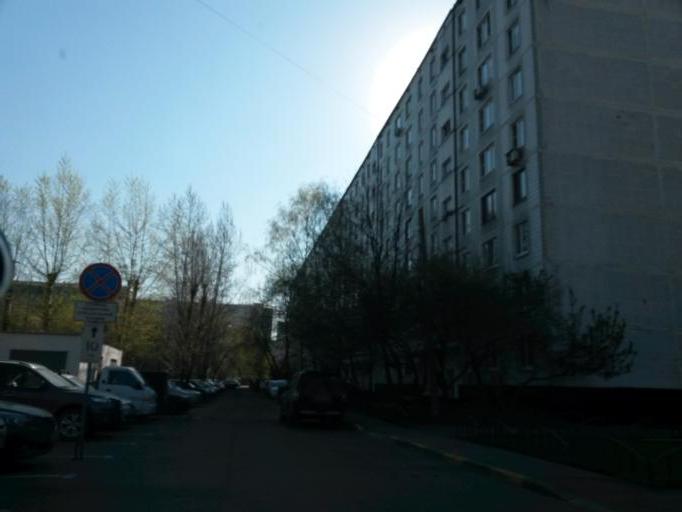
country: RU
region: Moscow
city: Mar'ino
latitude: 55.6484
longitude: 37.7194
